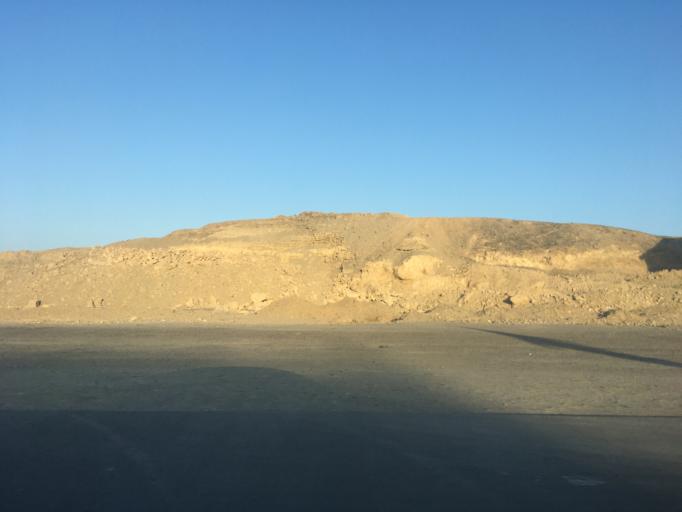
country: EG
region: Red Sea
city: Marsa Alam
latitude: 25.0667
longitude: 34.8917
